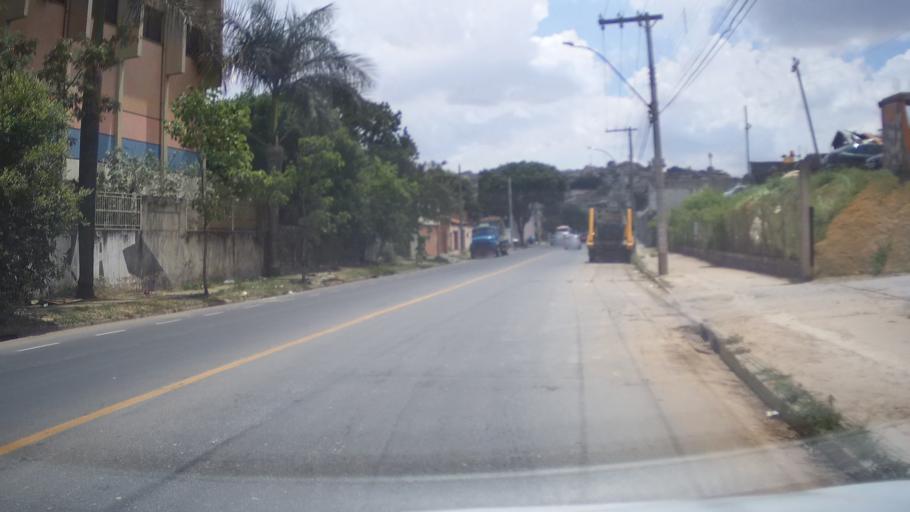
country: BR
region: Minas Gerais
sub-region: Contagem
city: Contagem
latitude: -19.9334
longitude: -44.0091
